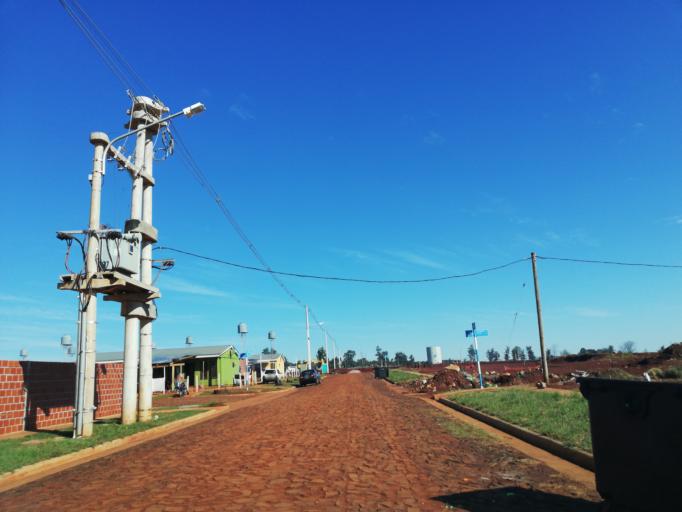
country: AR
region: Misiones
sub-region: Departamento de Capital
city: Posadas
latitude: -27.4149
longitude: -55.9918
